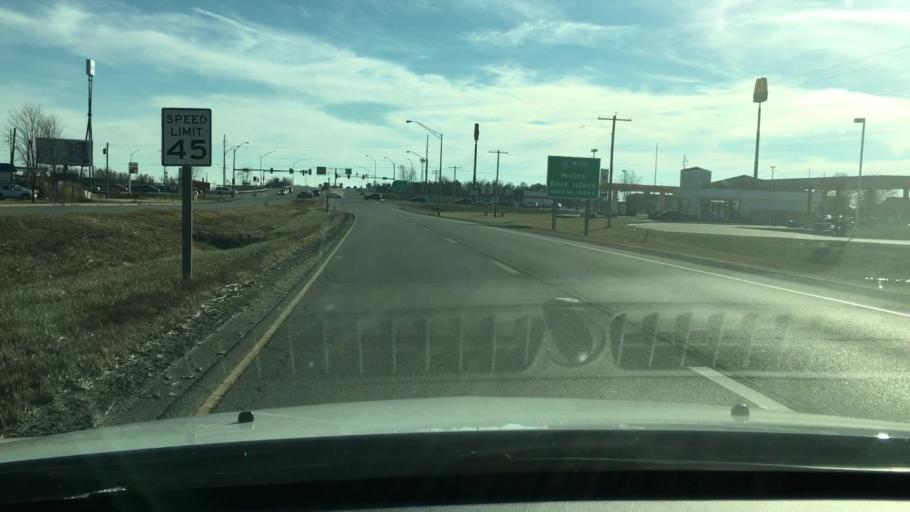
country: US
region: Illinois
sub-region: LaSalle County
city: Peru
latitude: 41.3702
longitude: -89.1258
